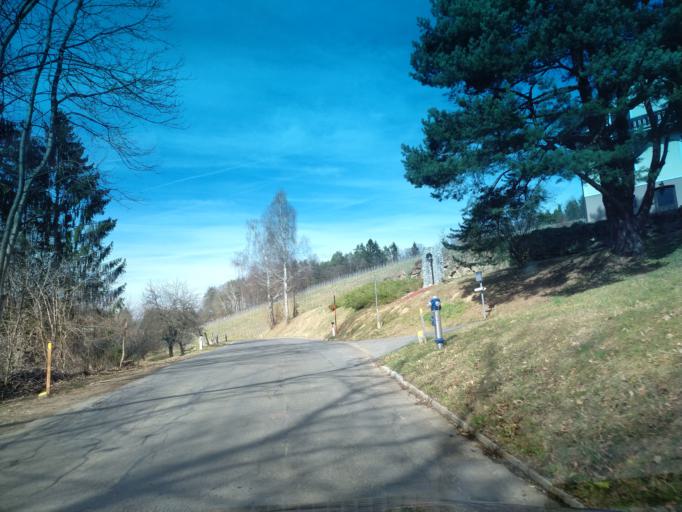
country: AT
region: Styria
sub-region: Politischer Bezirk Leibnitz
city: Sankt Nikolai im Sausal
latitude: 46.7989
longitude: 15.4310
